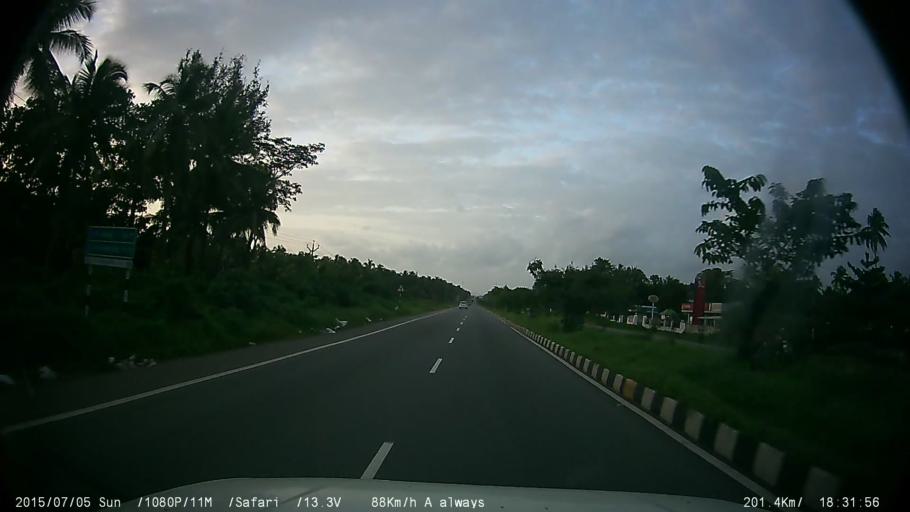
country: IN
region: Kerala
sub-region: Thrissur District
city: Trichur
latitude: 10.5015
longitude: 76.2581
